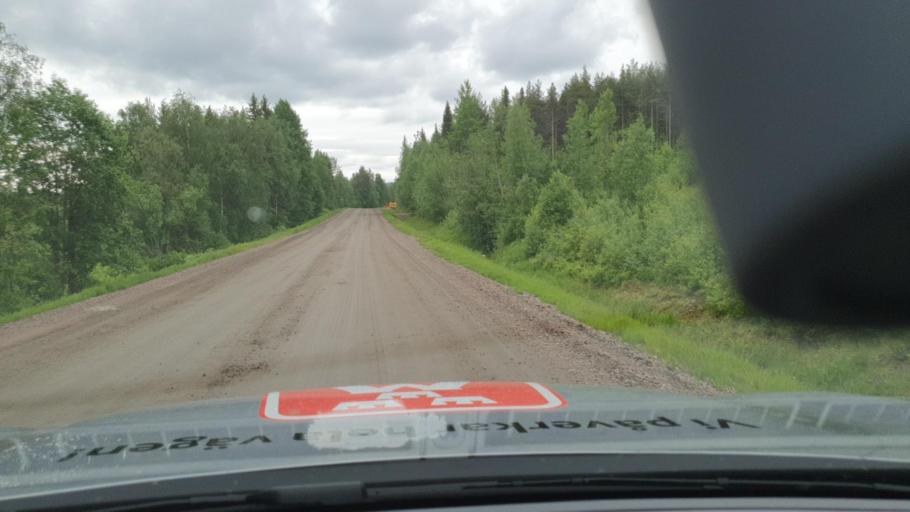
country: SE
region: Norrbotten
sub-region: Overtornea Kommun
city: OEvertornea
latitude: 66.4075
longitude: 23.6063
